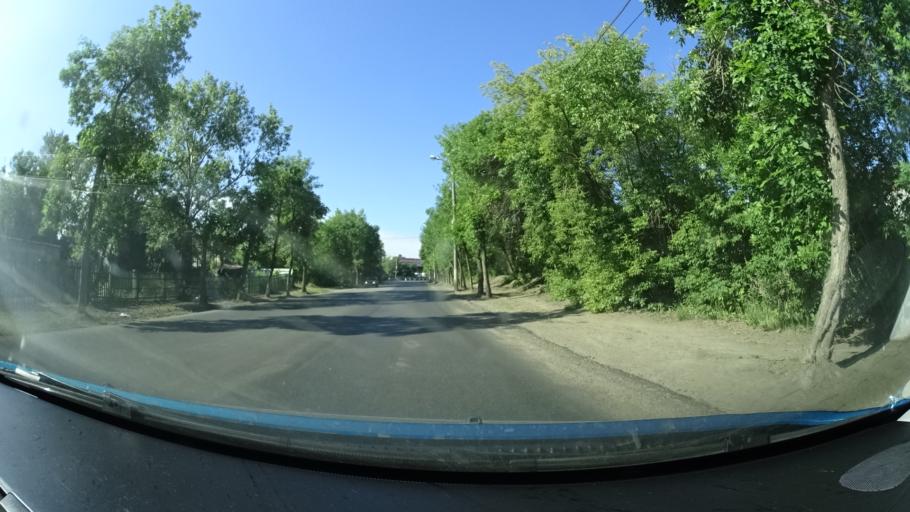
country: RU
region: Bashkortostan
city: Ufa
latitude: 54.8321
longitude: 56.0729
